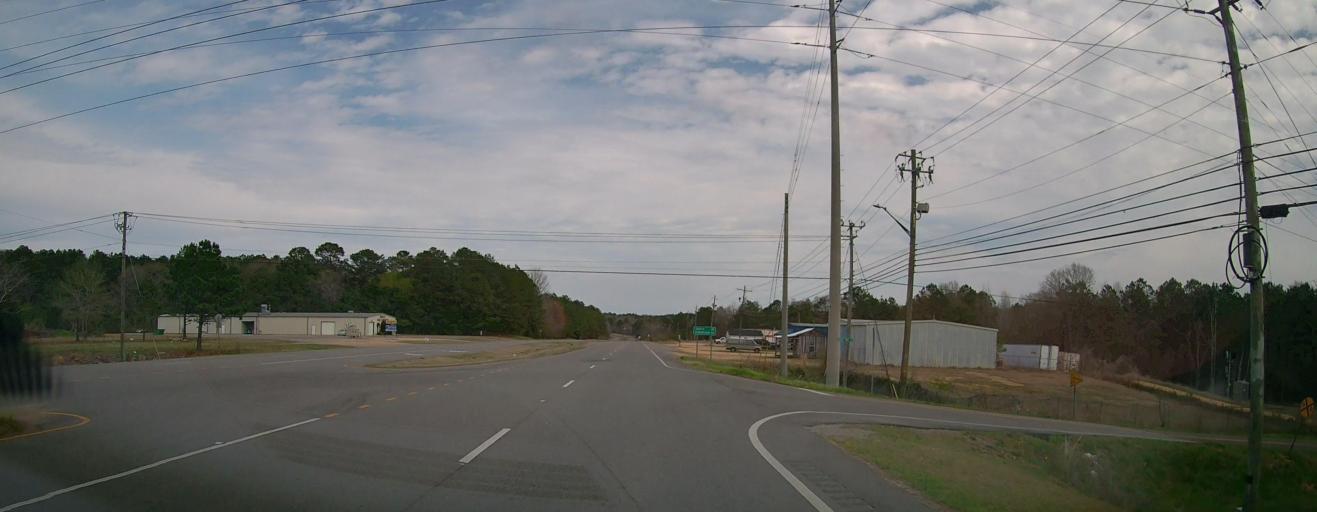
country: US
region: Alabama
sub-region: Marion County
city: Winfield
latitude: 33.9294
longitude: -87.7721
